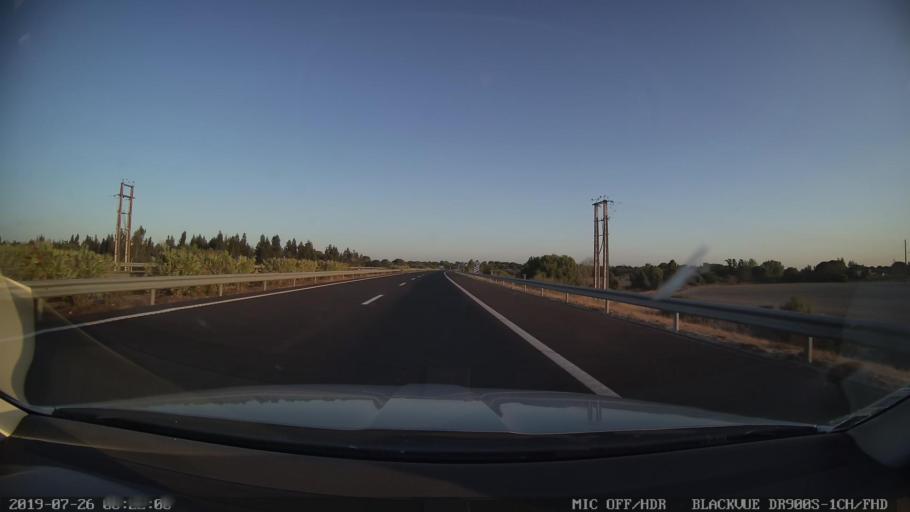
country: PT
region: Evora
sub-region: Vendas Novas
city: Vendas Novas
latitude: 38.6955
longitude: -8.6393
